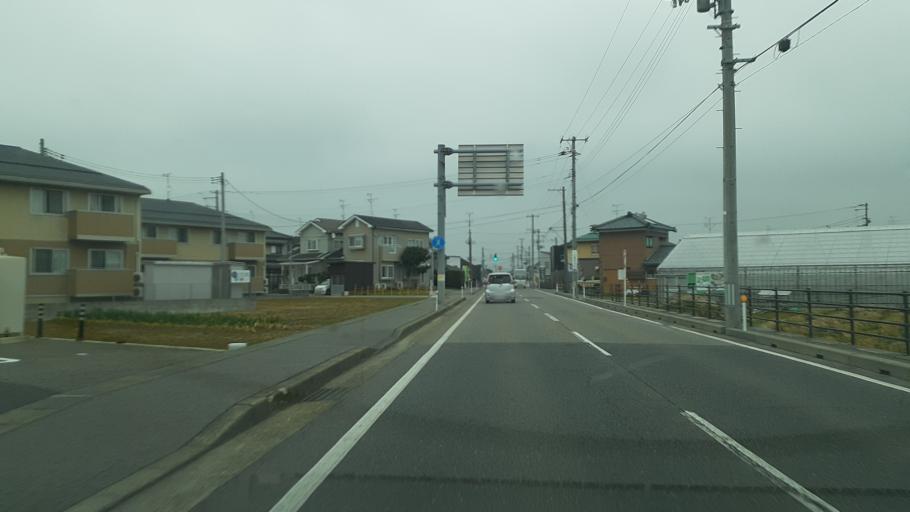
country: JP
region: Niigata
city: Niigata-shi
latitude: 37.8549
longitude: 139.0342
